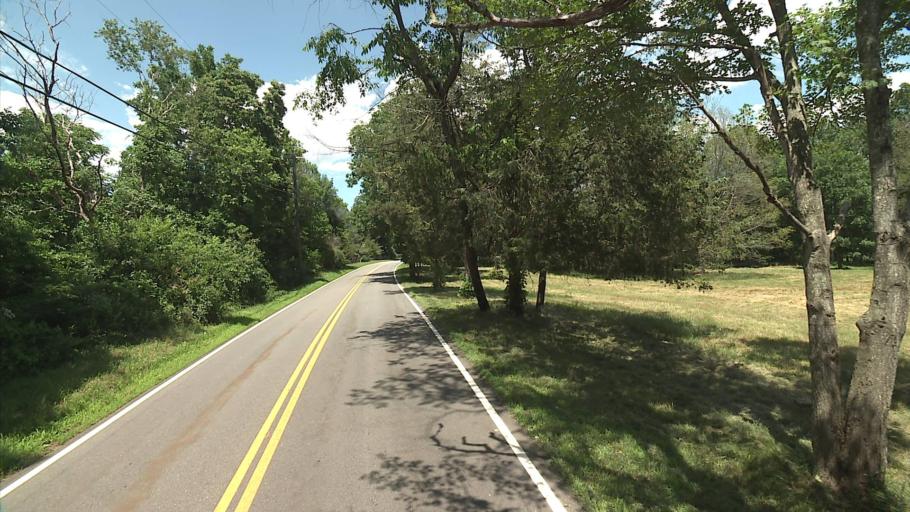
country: US
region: Connecticut
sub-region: Middlesex County
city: Essex Village
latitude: 41.4419
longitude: -72.3381
